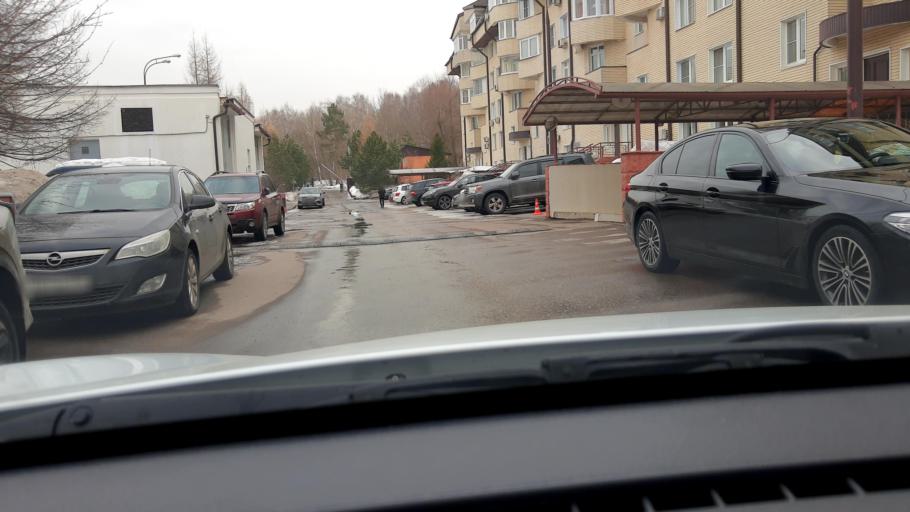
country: RU
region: Moscow
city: Rublevo
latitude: 55.7685
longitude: 37.3988
